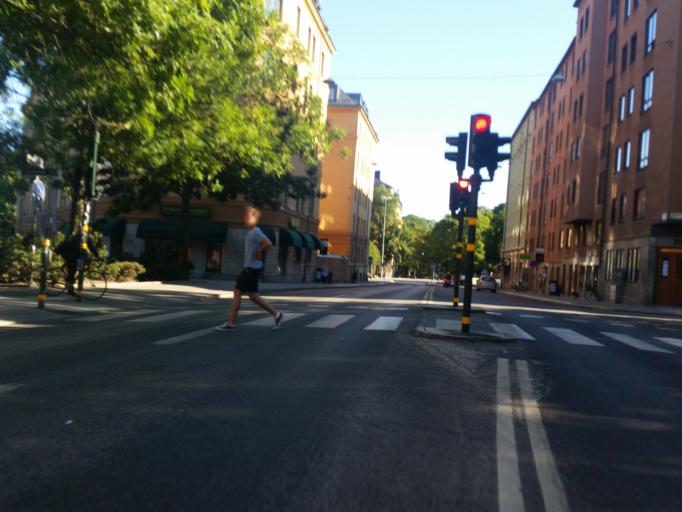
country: SE
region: Stockholm
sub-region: Stockholms Kommun
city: OEstermalm
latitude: 59.3111
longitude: 18.0858
